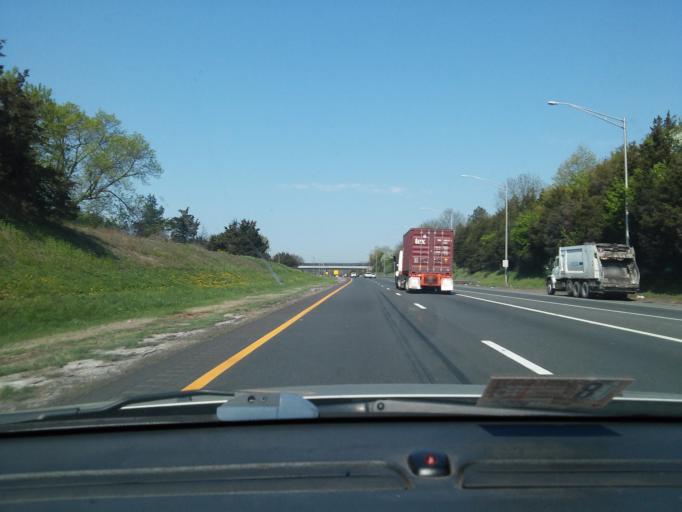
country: US
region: New Jersey
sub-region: Somerset County
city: Bedminster
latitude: 40.6434
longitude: -74.6506
